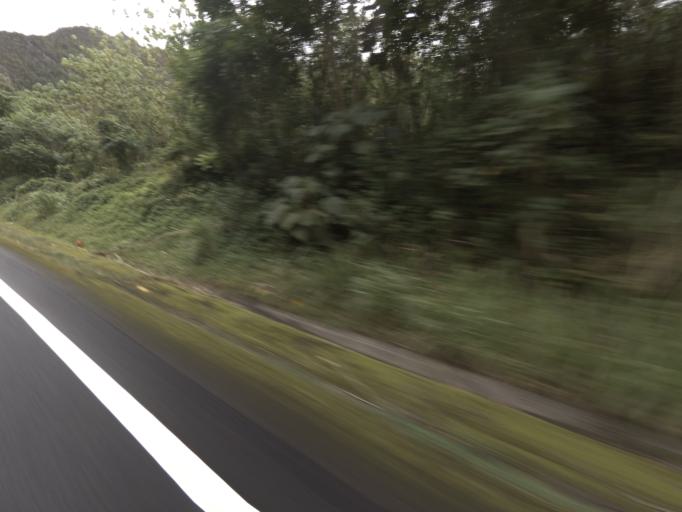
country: US
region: Hawaii
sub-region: Honolulu County
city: Kane'ohe
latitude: 21.3898
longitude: -157.8170
